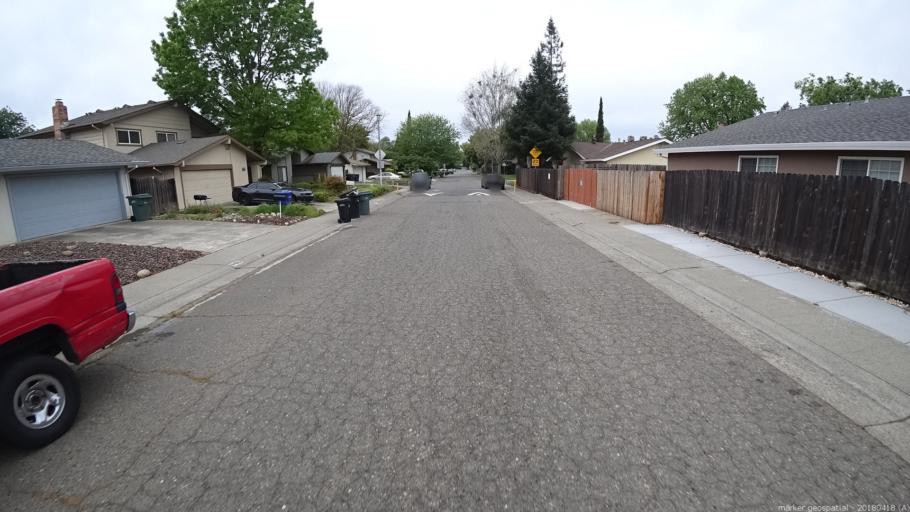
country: US
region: California
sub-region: Sacramento County
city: La Riviera
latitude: 38.5707
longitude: -121.3468
